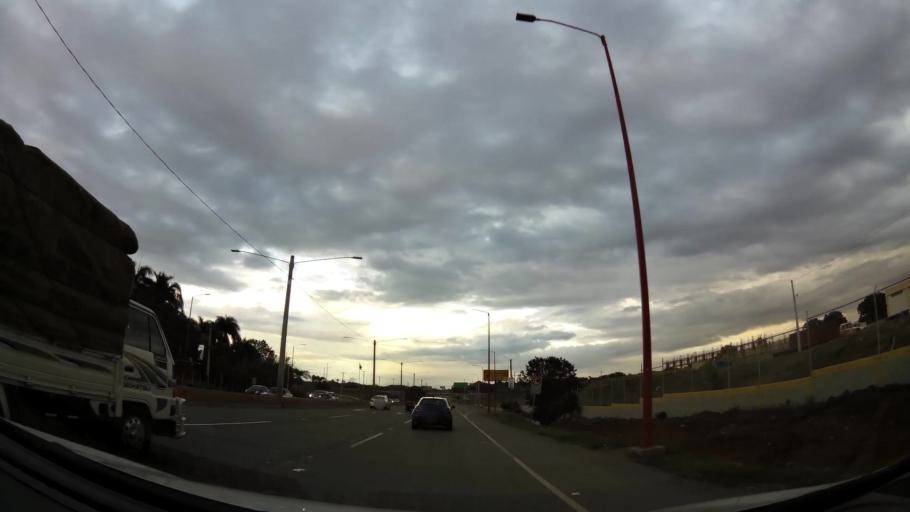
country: DO
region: Santo Domingo
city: Santo Domingo Oeste
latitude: 18.5633
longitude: -70.0726
